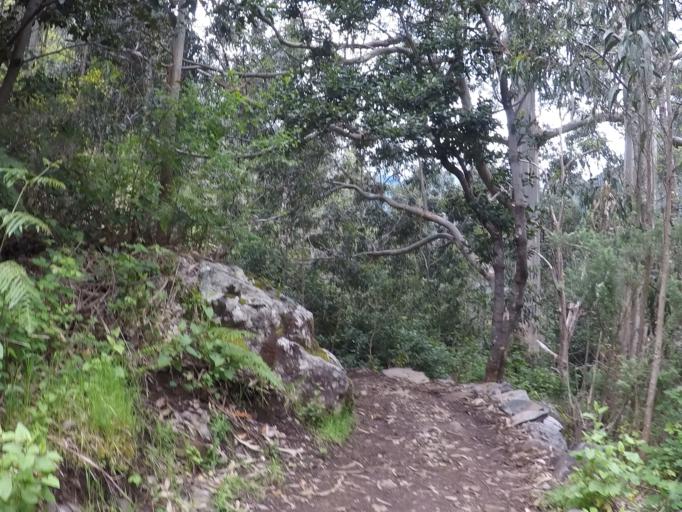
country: PT
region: Madeira
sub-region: Camara de Lobos
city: Curral das Freiras
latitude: 32.7445
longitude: -16.9998
